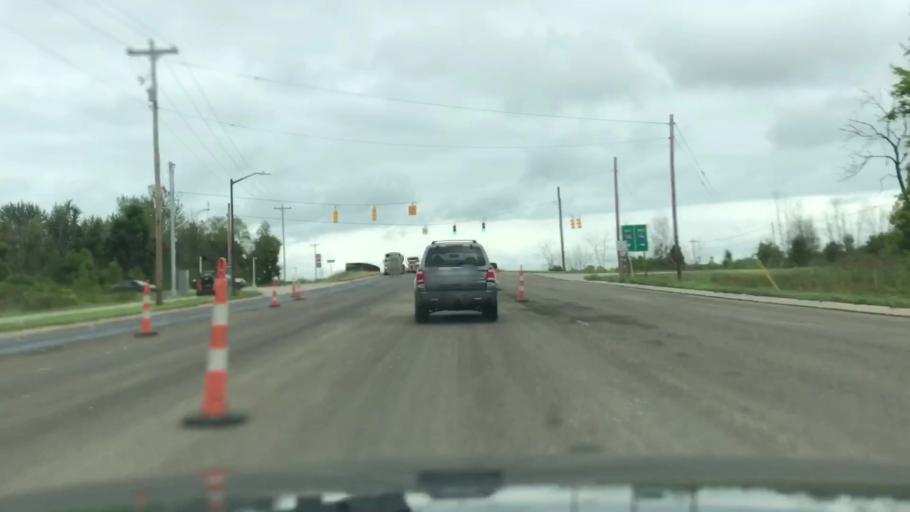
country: US
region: Michigan
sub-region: Ottawa County
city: Zeeland
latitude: 42.7833
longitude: -86.0304
